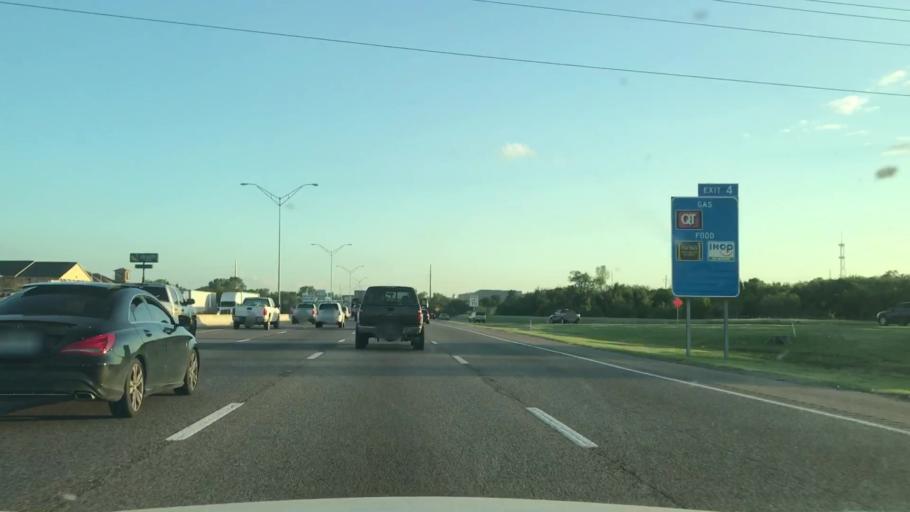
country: US
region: Texas
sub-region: Dallas County
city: Mesquite
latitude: 32.7804
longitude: -96.6234
